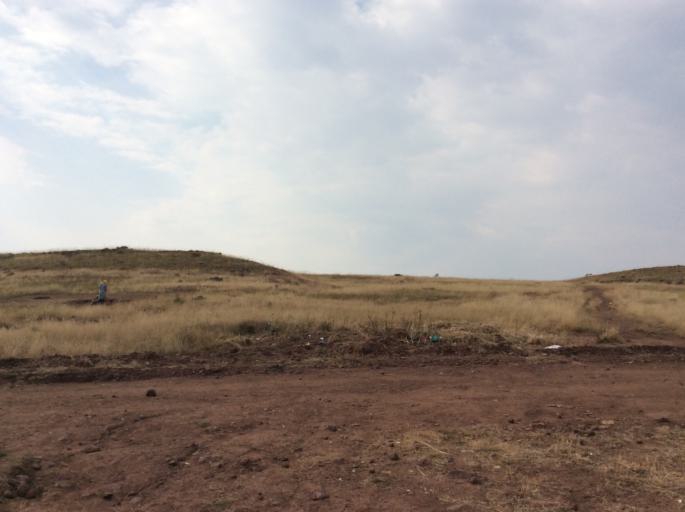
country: LS
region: Mafeteng
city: Mafeteng
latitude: -29.9863
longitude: 27.0023
